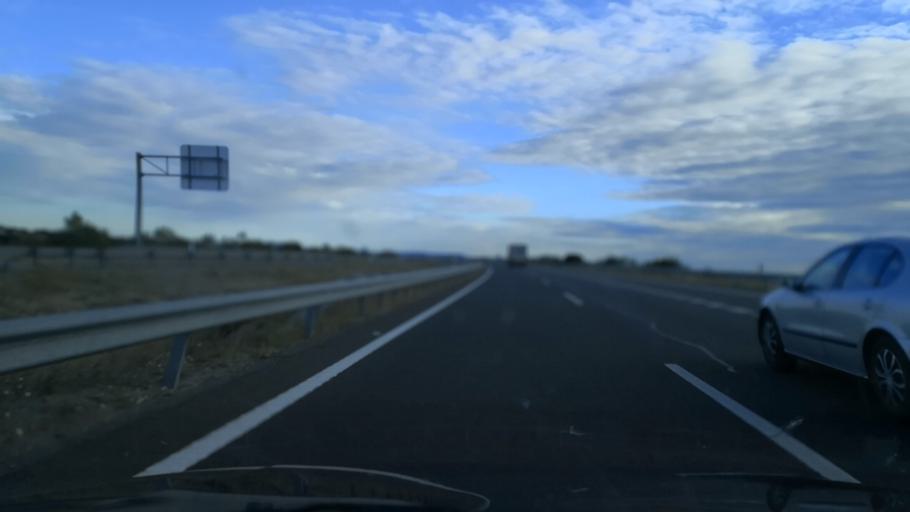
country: ES
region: Extremadura
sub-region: Provincia de Caceres
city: Santiago del Campo
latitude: 39.6486
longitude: -6.3949
